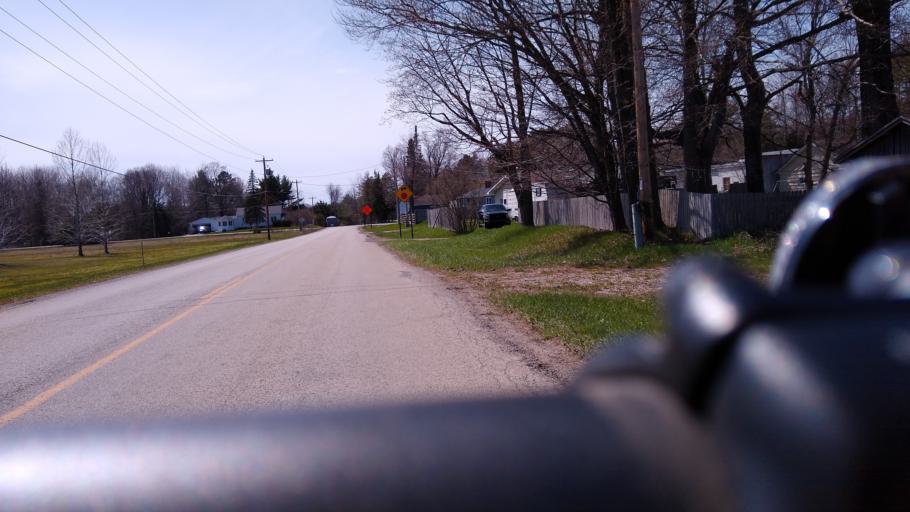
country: US
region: Michigan
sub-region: Delta County
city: Escanaba
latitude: 45.7352
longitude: -87.1857
